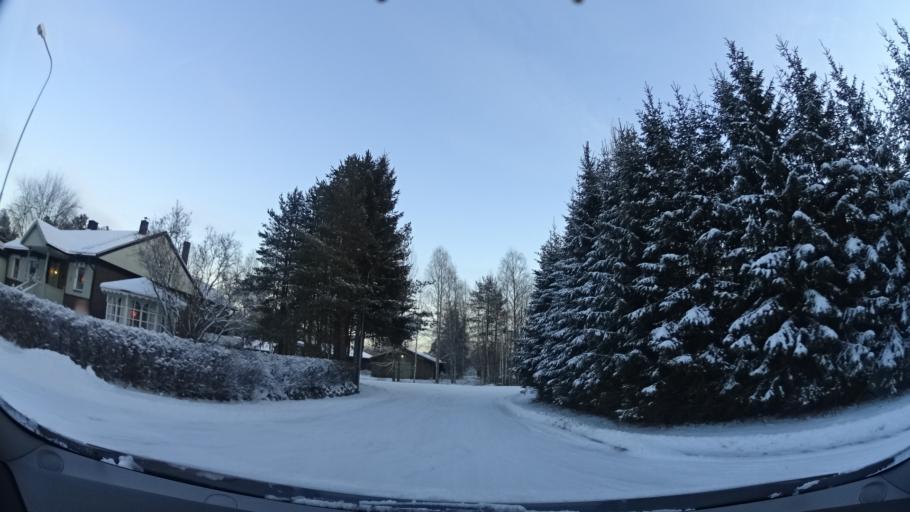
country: SE
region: Vaesterbotten
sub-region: Skelleftea Kommun
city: Kage
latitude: 64.8411
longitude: 20.9847
